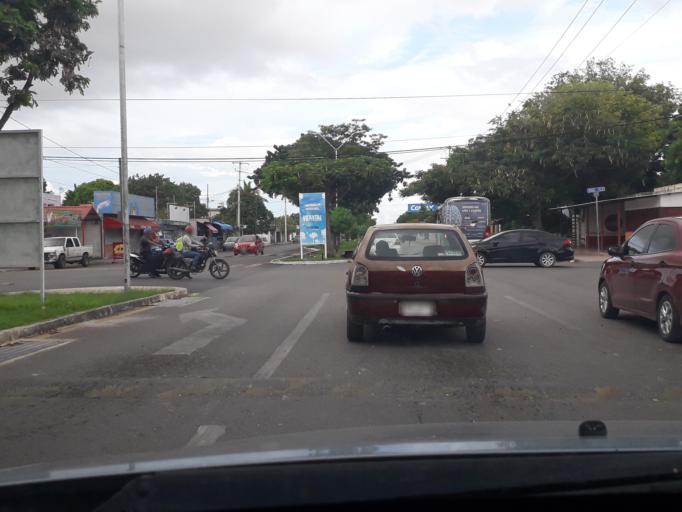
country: MX
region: Yucatan
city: Merida
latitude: 20.9644
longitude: -89.6636
